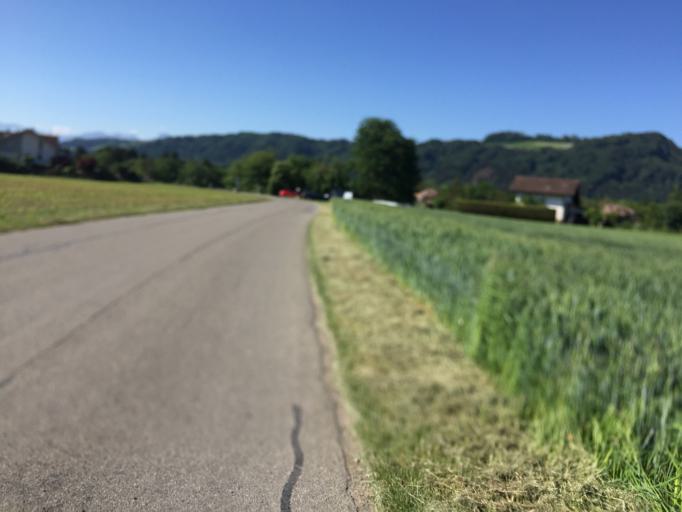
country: CH
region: Bern
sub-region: Bern-Mittelland District
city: Rubigen
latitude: 46.8965
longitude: 7.5385
